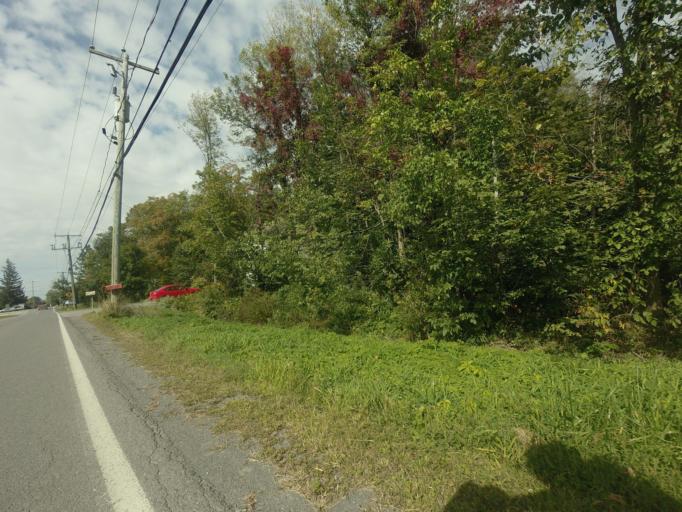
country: CA
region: Quebec
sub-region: Laurentides
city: Blainville
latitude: 45.6221
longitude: -73.9113
